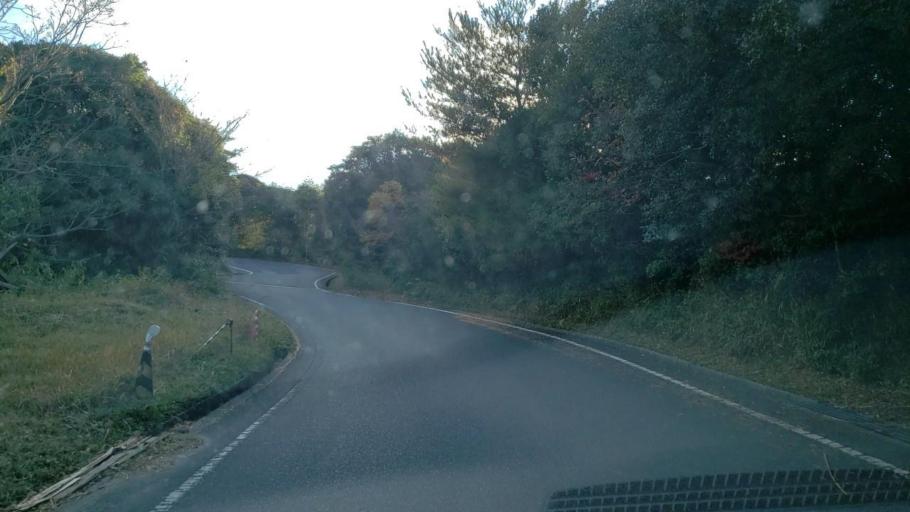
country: JP
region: Hyogo
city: Akashi
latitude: 34.5411
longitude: 134.9632
